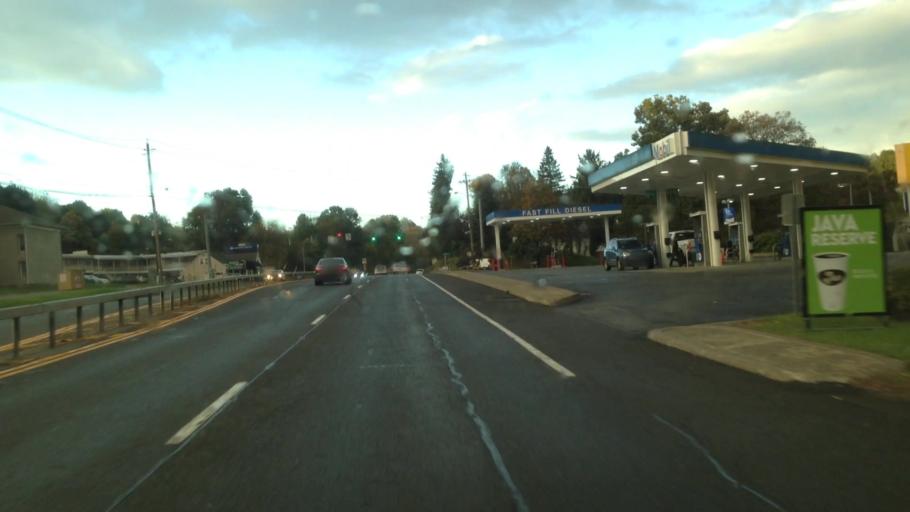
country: US
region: New York
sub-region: Ulster County
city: Highland
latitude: 41.7276
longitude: -73.9615
